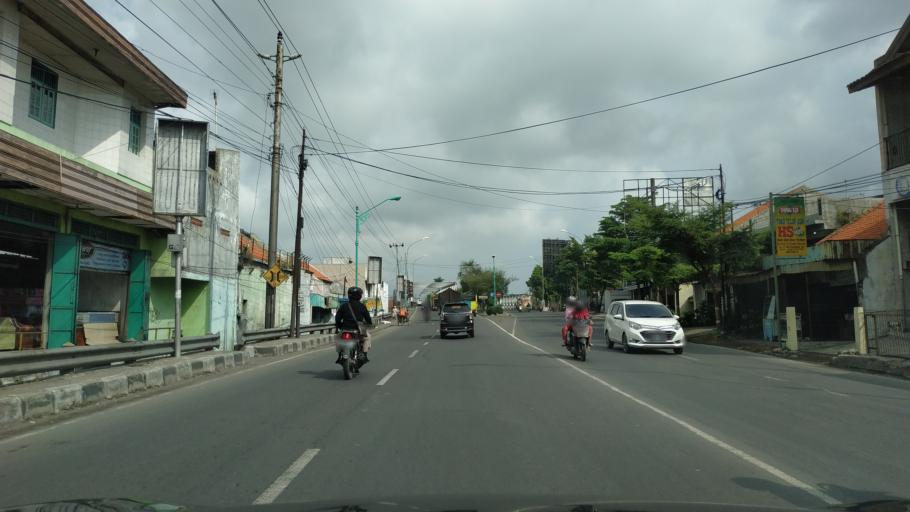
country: ID
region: Central Java
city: Dukuhturi
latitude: -6.8699
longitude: 109.0359
